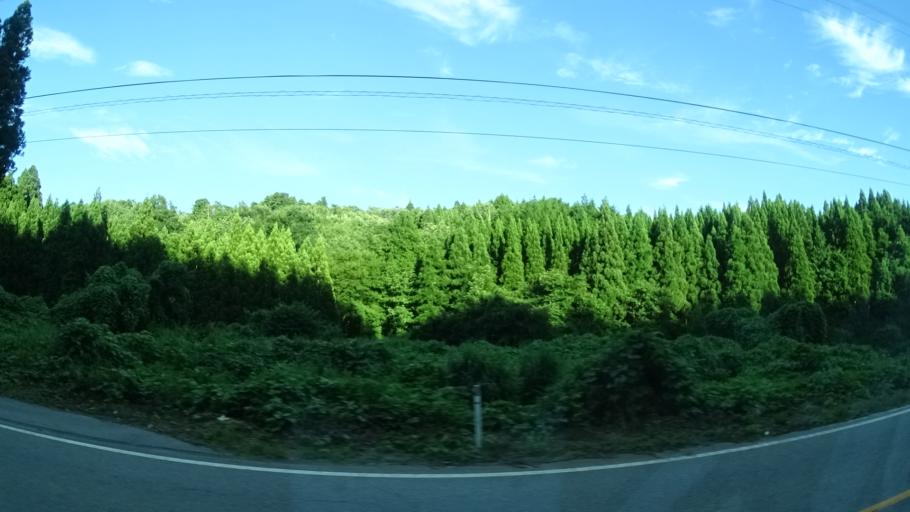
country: JP
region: Ishikawa
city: Nanao
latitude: 37.2842
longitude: 136.8882
